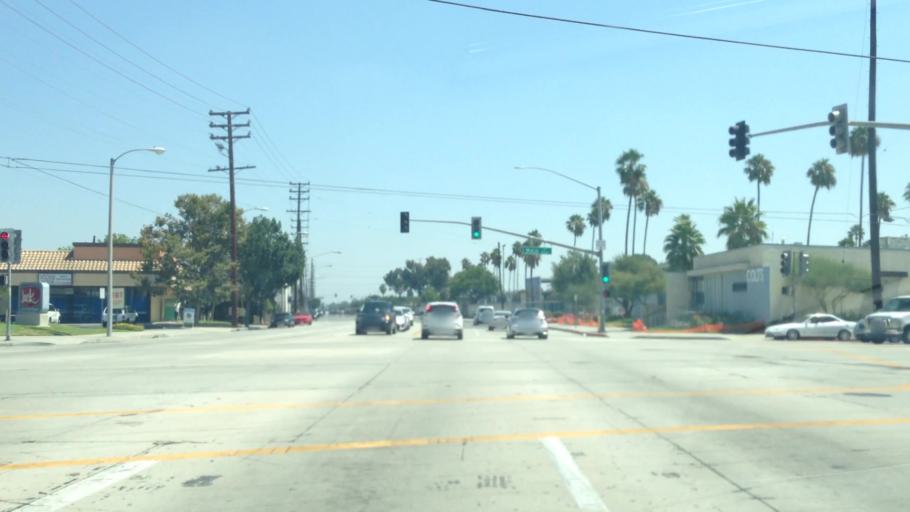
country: US
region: California
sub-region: Los Angeles County
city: Carson
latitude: 33.8243
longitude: -118.2764
